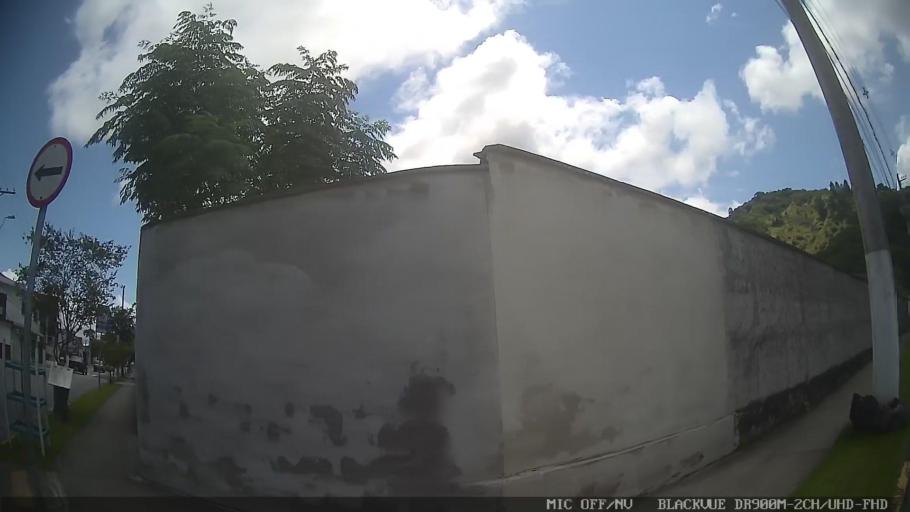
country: BR
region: Sao Paulo
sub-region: Caraguatatuba
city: Caraguatatuba
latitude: -23.6190
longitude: -45.4098
